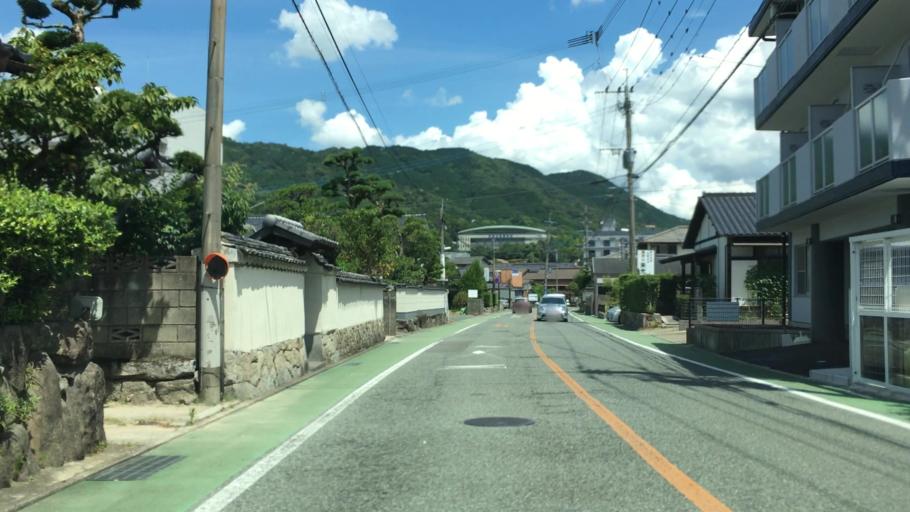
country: JP
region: Fukuoka
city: Dazaifu
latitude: 33.5142
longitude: 130.5267
